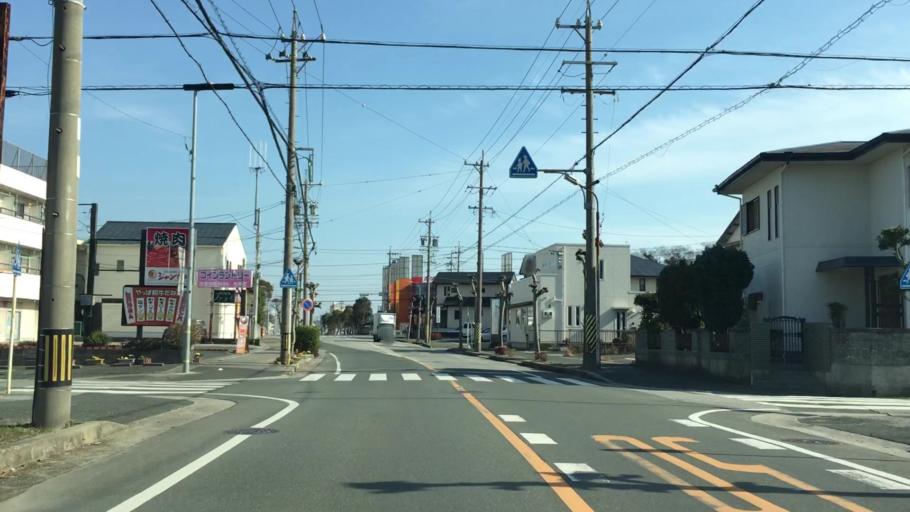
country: JP
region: Aichi
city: Tahara
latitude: 34.6682
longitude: 137.2614
